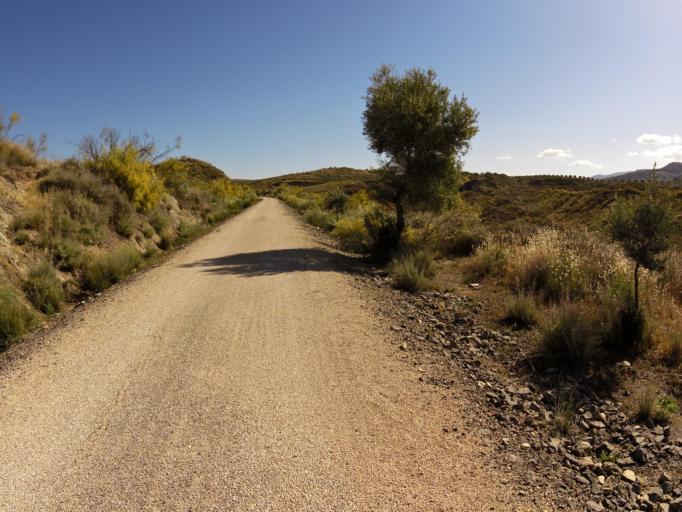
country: ES
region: Andalusia
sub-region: Provincia de Jaen
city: Alcaudete
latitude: 37.5941
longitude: -4.1572
